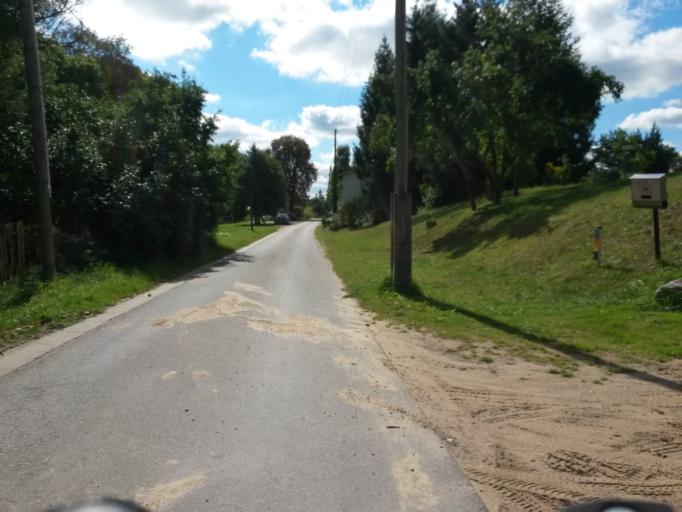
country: DE
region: Brandenburg
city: Mittenwalde
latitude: 53.1943
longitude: 13.6055
